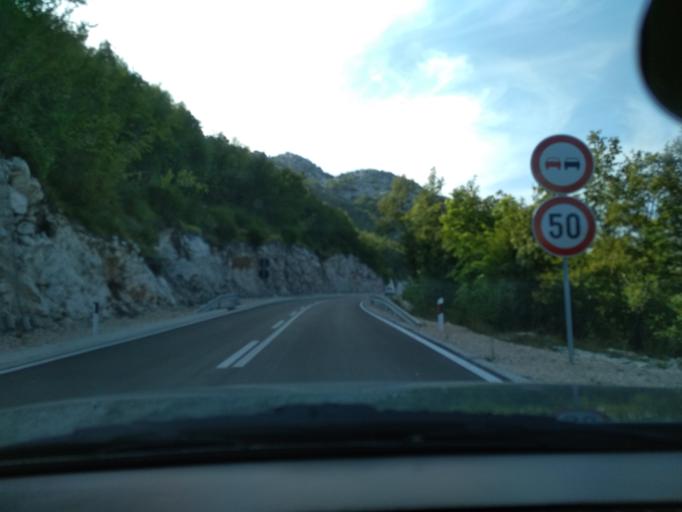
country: ME
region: Cetinje
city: Cetinje
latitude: 42.4184
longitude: 18.8766
